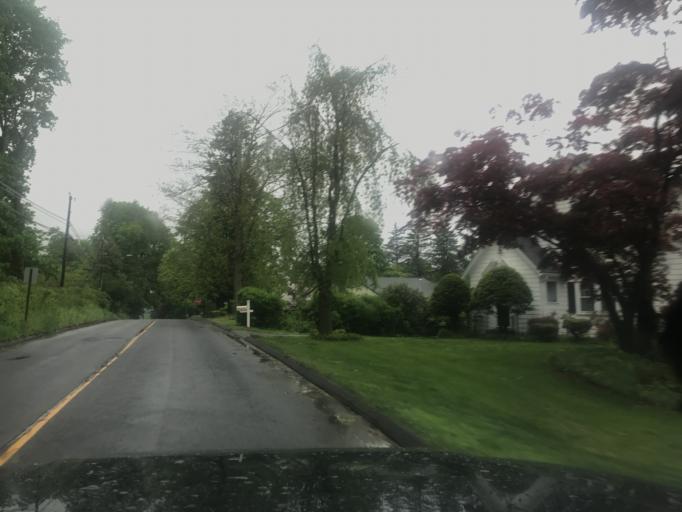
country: US
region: Connecticut
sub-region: Fairfield County
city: Bethel
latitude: 41.3711
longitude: -73.3967
